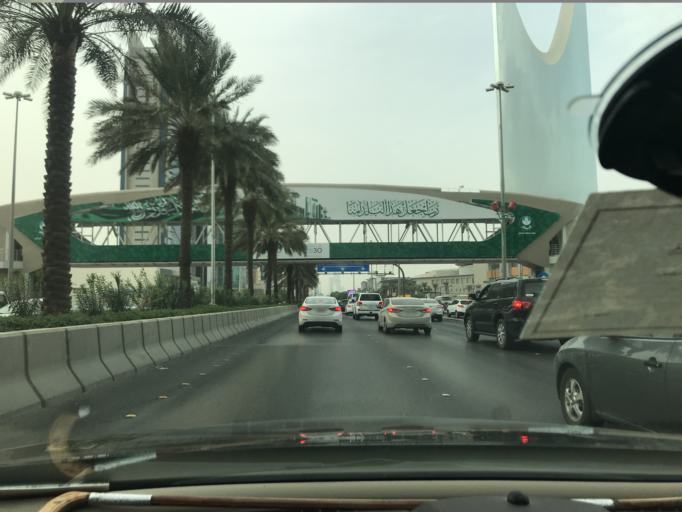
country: SA
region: Ar Riyad
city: Riyadh
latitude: 24.7071
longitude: 46.6747
